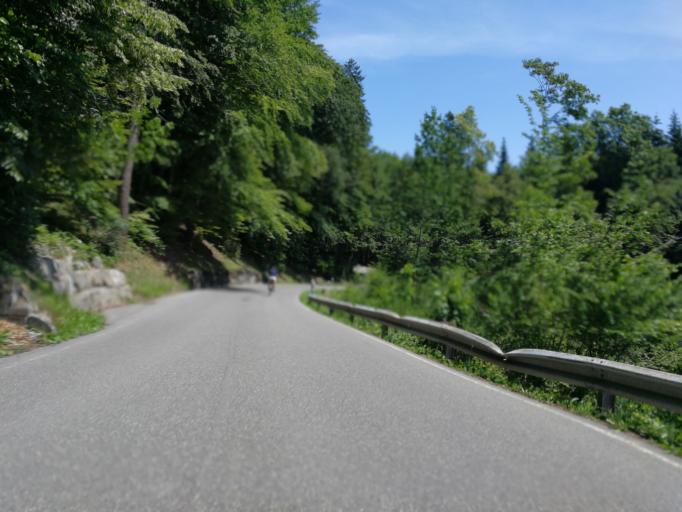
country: CH
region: Saint Gallen
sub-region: Wahlkreis See-Gaster
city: Eschenbach
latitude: 47.2280
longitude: 8.9222
